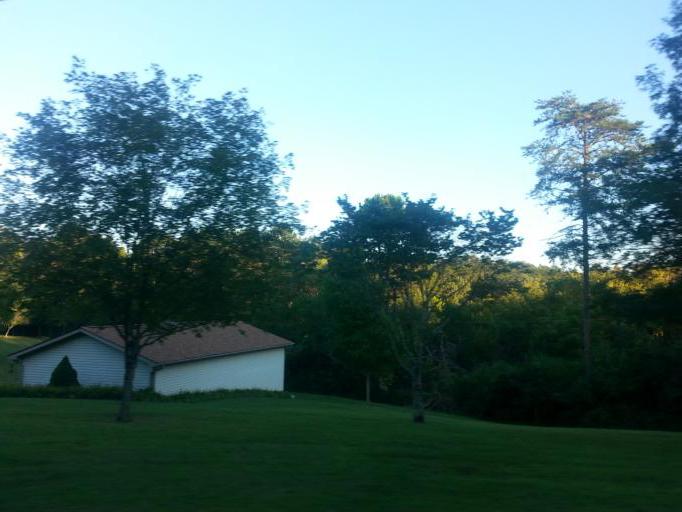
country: US
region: Tennessee
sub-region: Knox County
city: Knoxville
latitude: 35.9002
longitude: -83.8451
